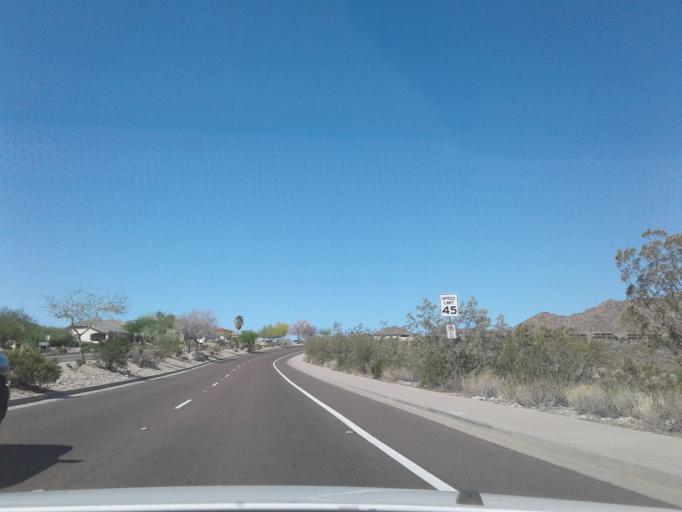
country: US
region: Arizona
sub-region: Maricopa County
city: Fountain Hills
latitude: 33.6042
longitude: -111.7526
